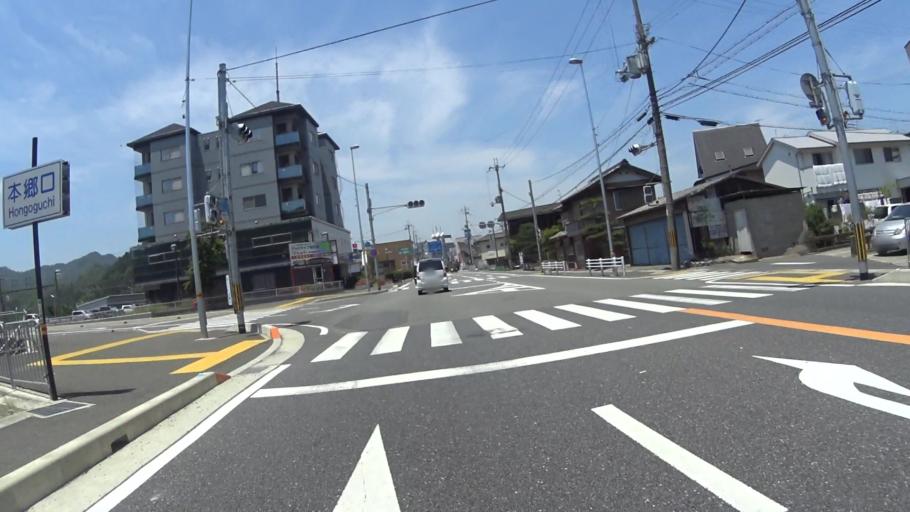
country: JP
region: Kyoto
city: Kameoka
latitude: 35.0684
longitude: 135.5347
